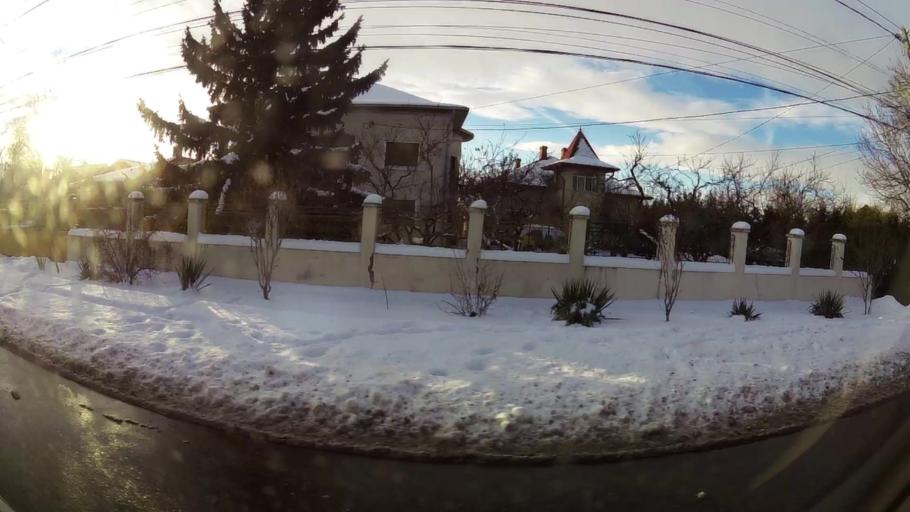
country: RO
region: Ilfov
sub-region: Comuna Jilava
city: Jilava
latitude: 44.3381
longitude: 26.0832
